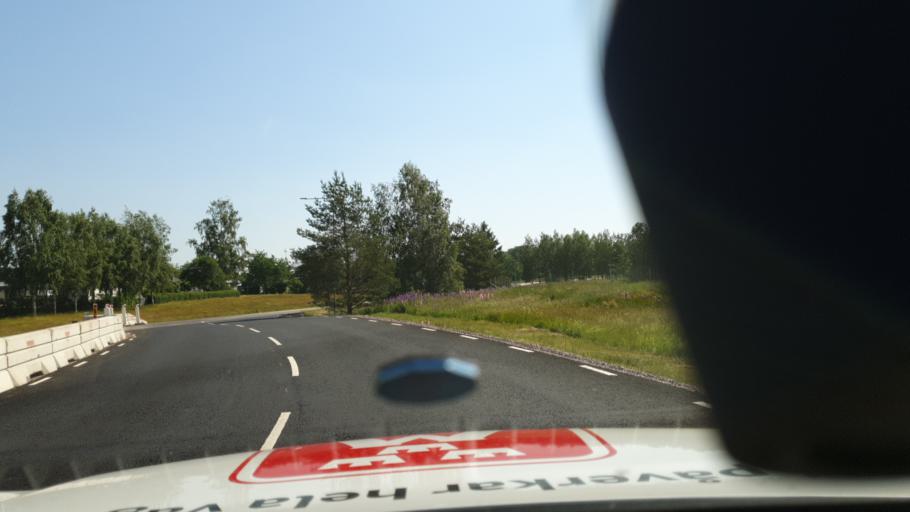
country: SE
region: Vaestra Goetaland
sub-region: Tibro Kommun
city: Tibro
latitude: 58.4134
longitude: 14.1550
